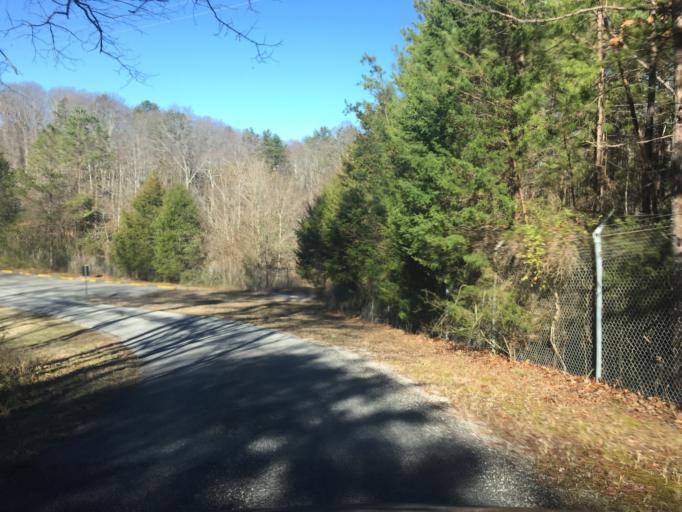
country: US
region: Tennessee
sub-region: Hamilton County
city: Harrison
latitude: 35.0986
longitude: -85.1153
